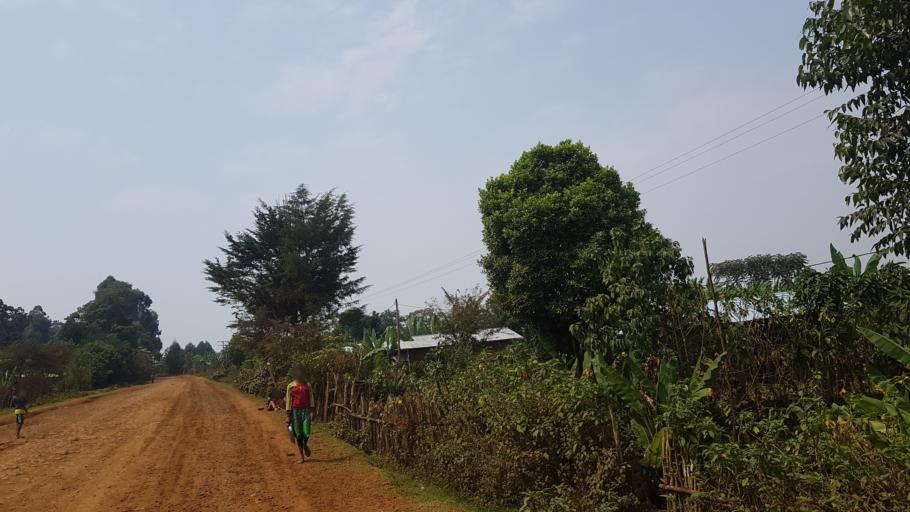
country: ET
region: Oromiya
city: Gore
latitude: 7.8032
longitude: 35.4574
